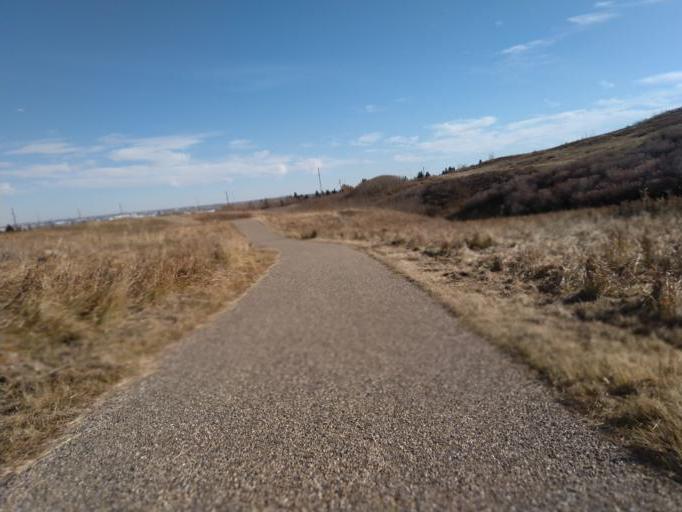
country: CA
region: Alberta
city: Calgary
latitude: 51.1231
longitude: -114.0994
